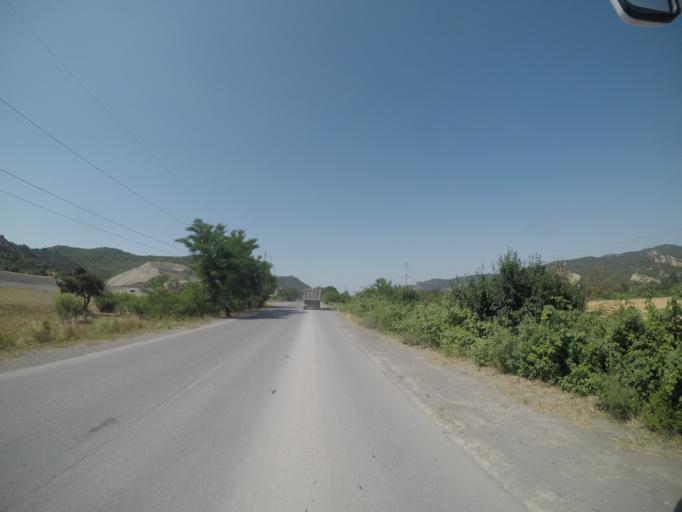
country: AZ
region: Agdas
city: Agdas
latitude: 40.7428
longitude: 47.5842
